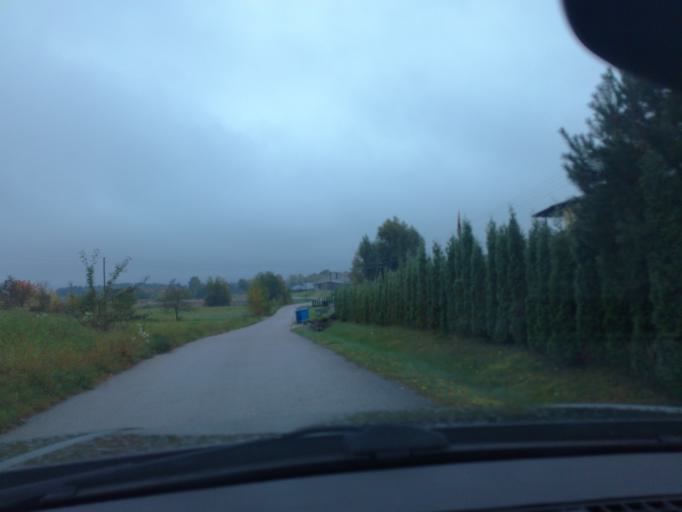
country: LT
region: Alytaus apskritis
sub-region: Alytus
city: Alytus
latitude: 54.4064
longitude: 24.0916
